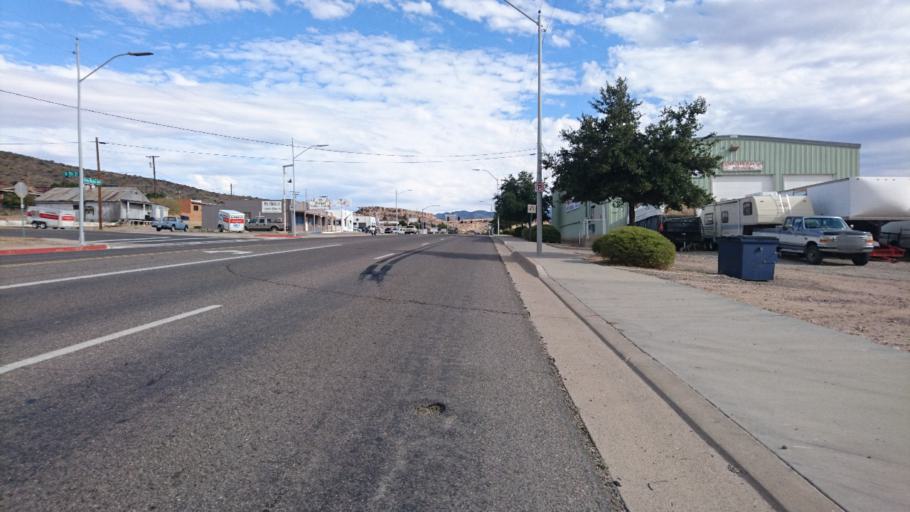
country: US
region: Arizona
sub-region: Mohave County
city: Kingman
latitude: 35.1877
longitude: -114.0480
